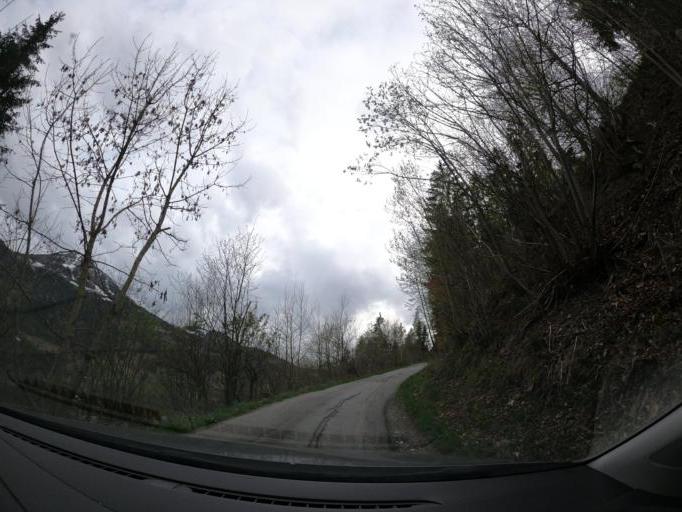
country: AT
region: Salzburg
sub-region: Politischer Bezirk Zell am See
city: Lend
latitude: 47.3020
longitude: 13.0606
